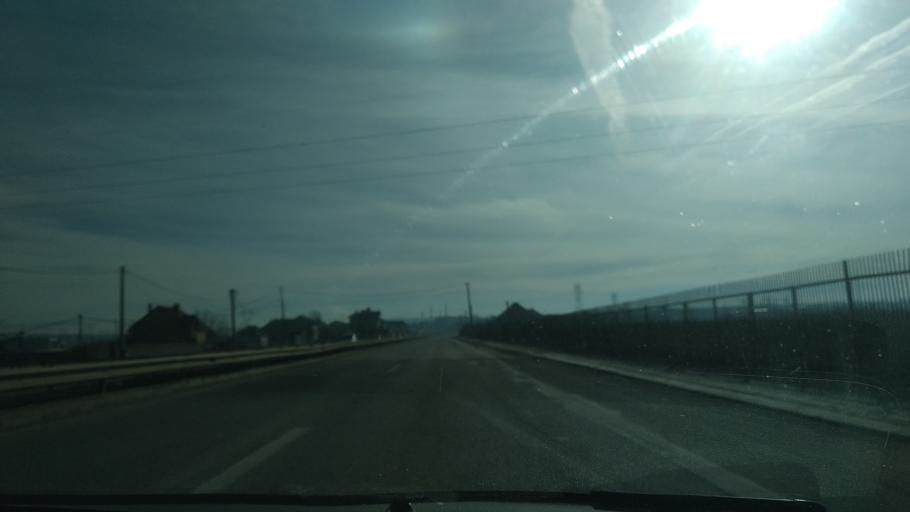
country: XK
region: Pristina
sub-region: Komuna e Obiliqit
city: Obiliq
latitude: 42.7097
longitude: 21.1026
